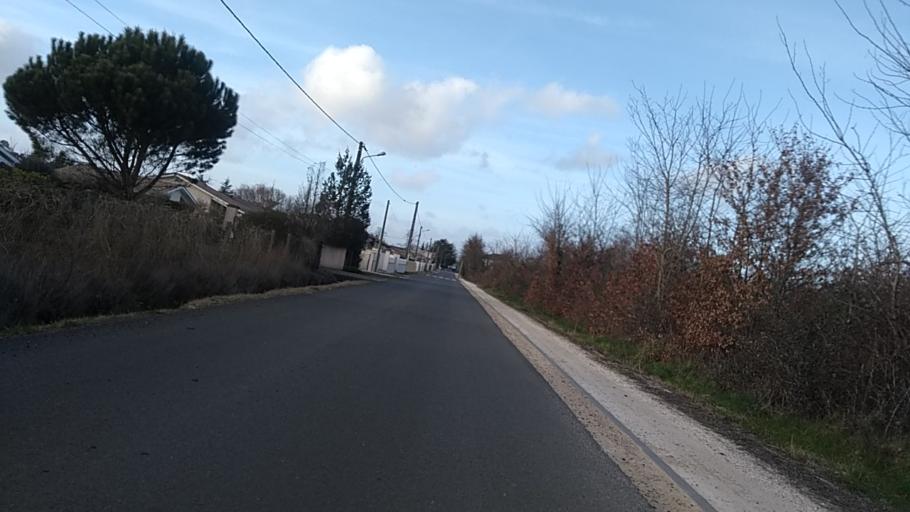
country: FR
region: Aquitaine
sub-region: Departement de la Gironde
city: Le Barp
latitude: 44.5986
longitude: -0.7683
